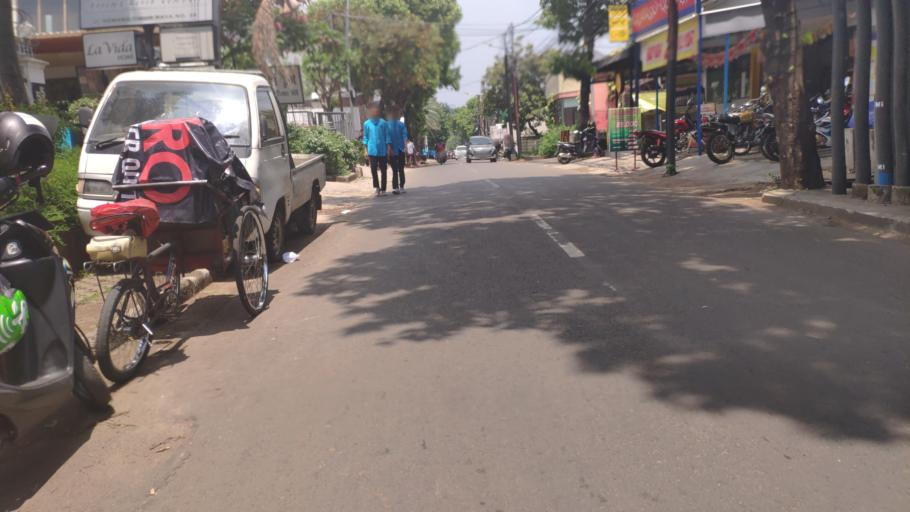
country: ID
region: Jakarta Raya
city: Jakarta
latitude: -6.2671
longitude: 106.8238
